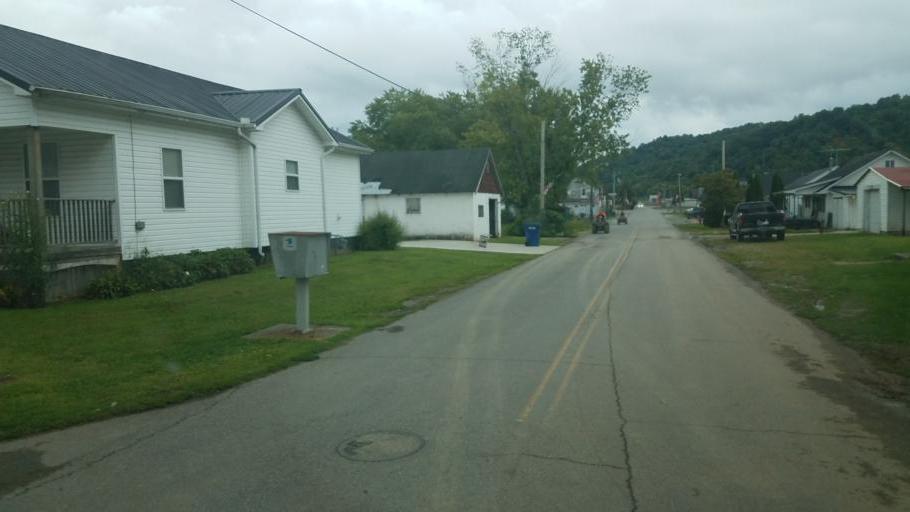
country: US
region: Kentucky
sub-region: Greenup County
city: South Shore
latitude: 38.7239
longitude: -82.9675
